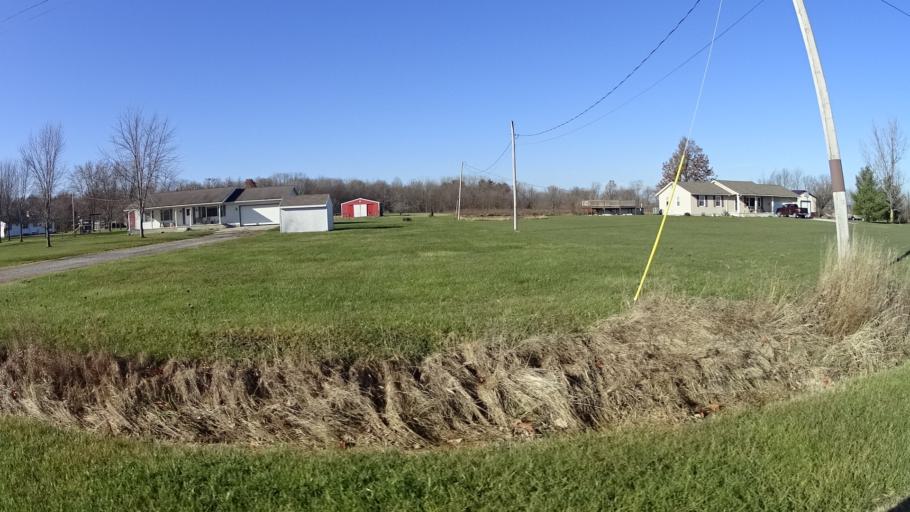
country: US
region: Ohio
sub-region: Lorain County
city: Wellington
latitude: 41.0960
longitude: -82.1809
